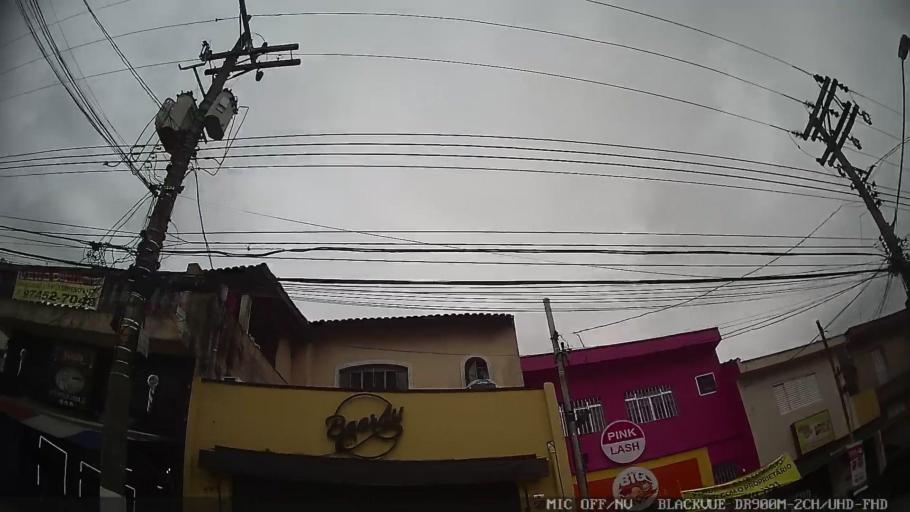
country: BR
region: Sao Paulo
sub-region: Osasco
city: Osasco
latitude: -23.5019
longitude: -46.7389
